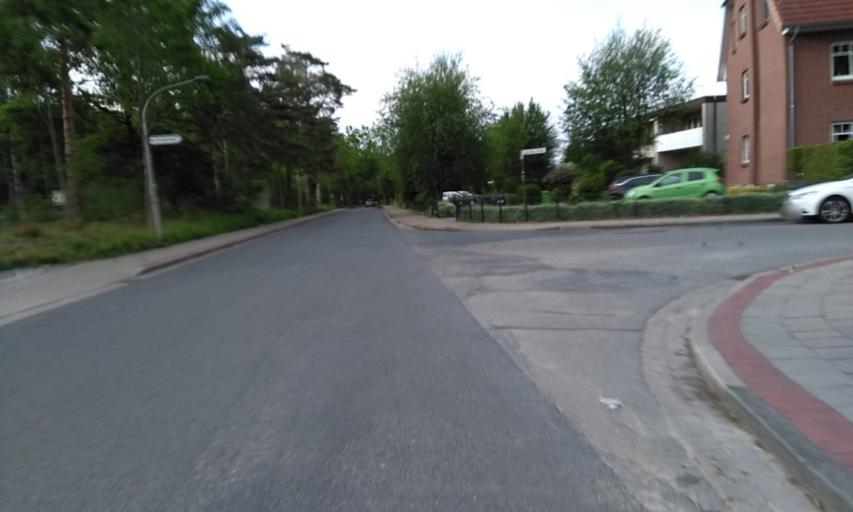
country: DE
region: Lower Saxony
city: Harsefeld
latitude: 53.4456
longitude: 9.4921
